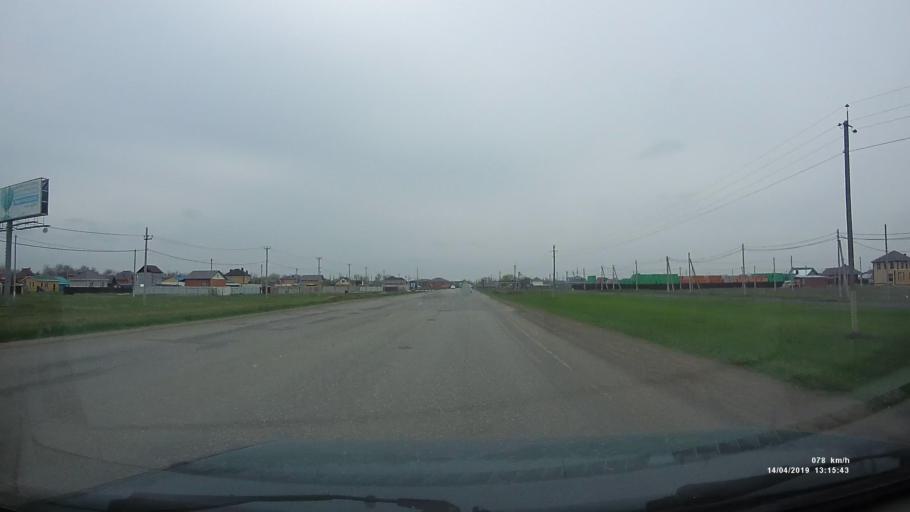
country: RU
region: Rostov
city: Kuleshovka
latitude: 47.0825
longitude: 39.5905
